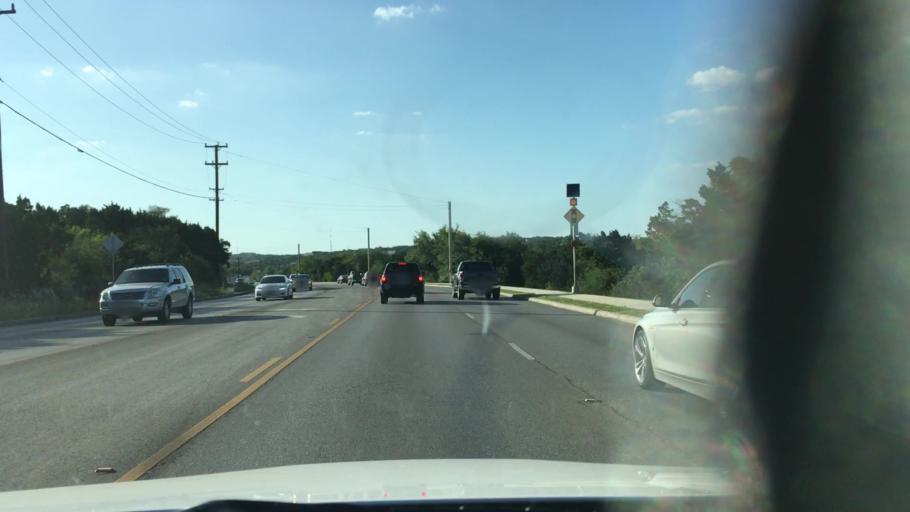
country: US
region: Texas
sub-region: Bexar County
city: Timberwood Park
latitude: 29.6584
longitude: -98.4329
